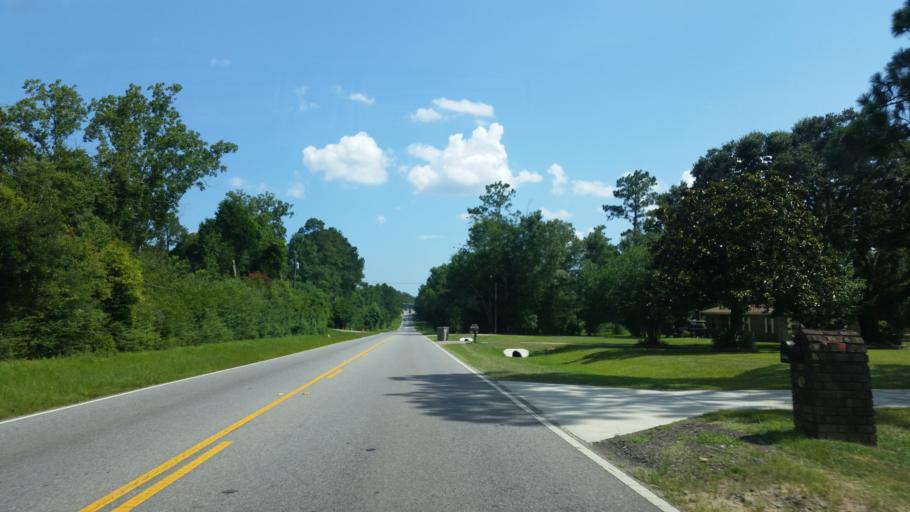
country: US
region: Florida
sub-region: Escambia County
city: Cantonment
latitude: 30.5420
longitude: -87.3804
